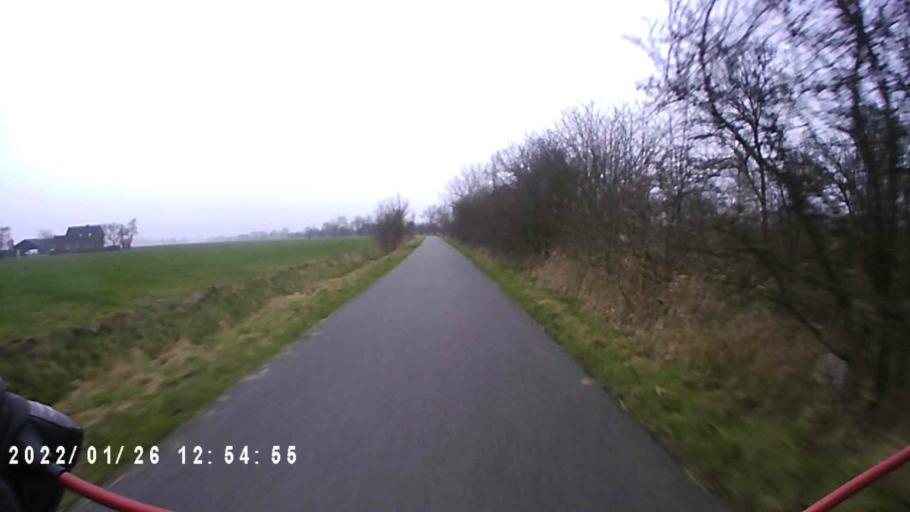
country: NL
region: Groningen
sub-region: Gemeente Winsum
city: Winsum
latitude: 53.3443
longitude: 6.4848
